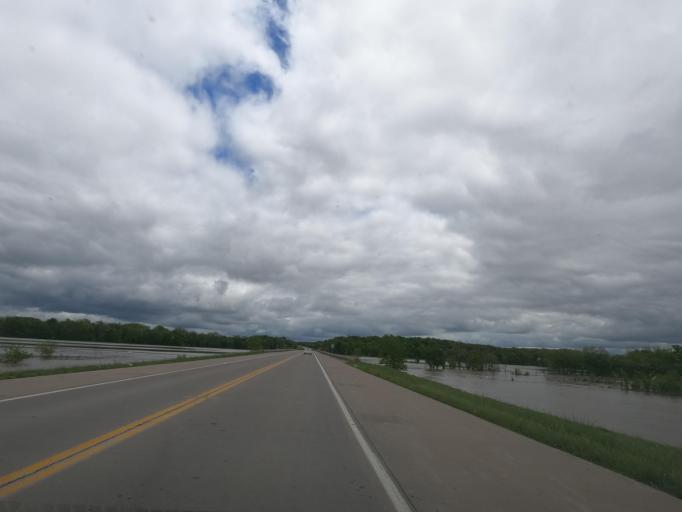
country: US
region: Kansas
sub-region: Wilson County
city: Neodesha
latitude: 37.3571
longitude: -95.6836
